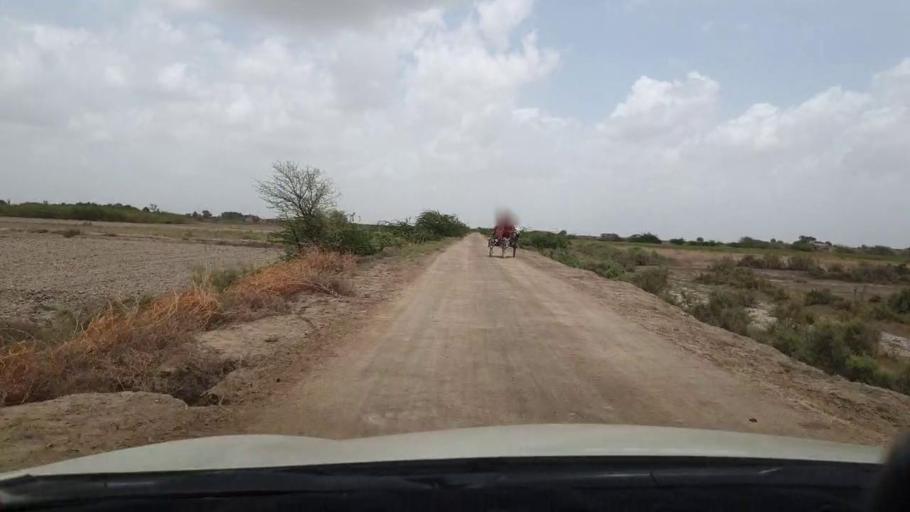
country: PK
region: Sindh
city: Kadhan
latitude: 24.3603
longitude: 68.9348
